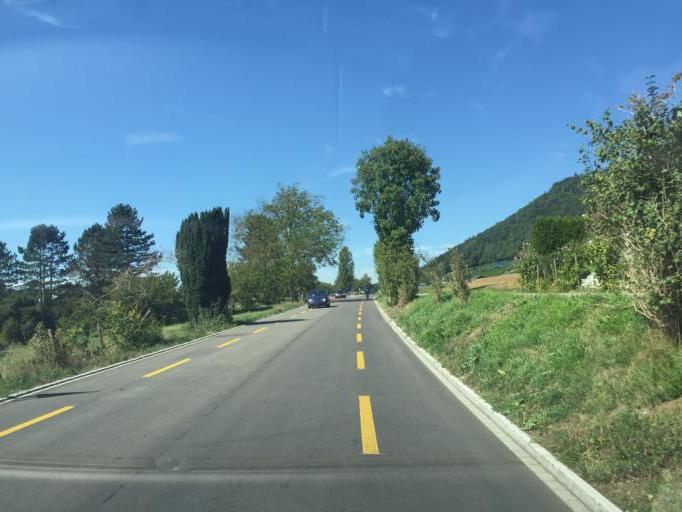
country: CH
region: Thurgau
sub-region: Frauenfeld District
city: Wagenhausen
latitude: 47.6657
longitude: 8.8477
